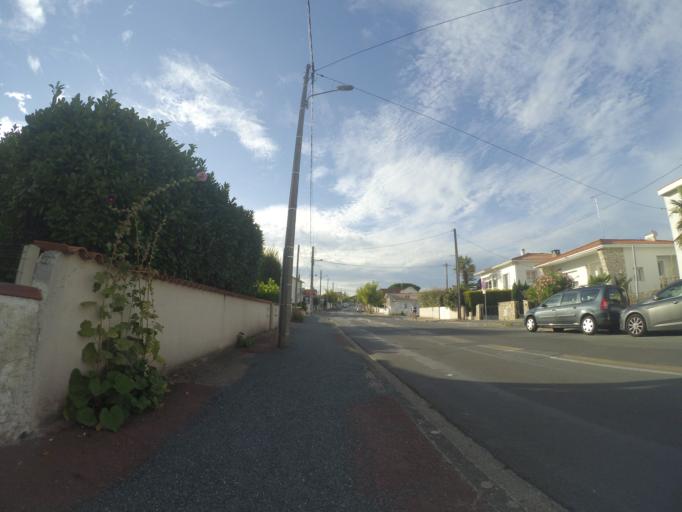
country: FR
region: Poitou-Charentes
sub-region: Departement de la Charente-Maritime
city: Saint-Georges-de-Didonne
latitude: 45.6036
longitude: -1.0036
